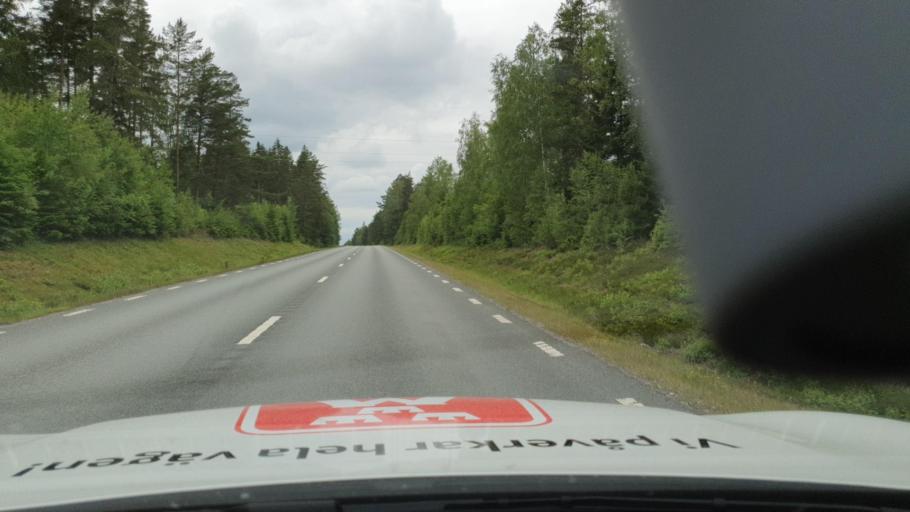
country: SE
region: Vaestra Goetaland
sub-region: Hjo Kommun
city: Hjo
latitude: 58.2275
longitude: 14.1584
